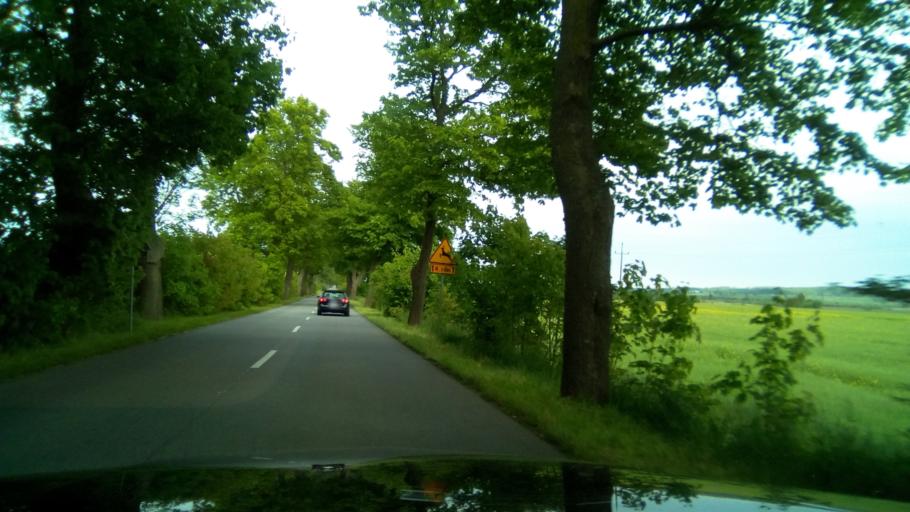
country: PL
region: Pomeranian Voivodeship
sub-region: Powiat pucki
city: Wierzchucino
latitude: 54.7899
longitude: 18.0133
